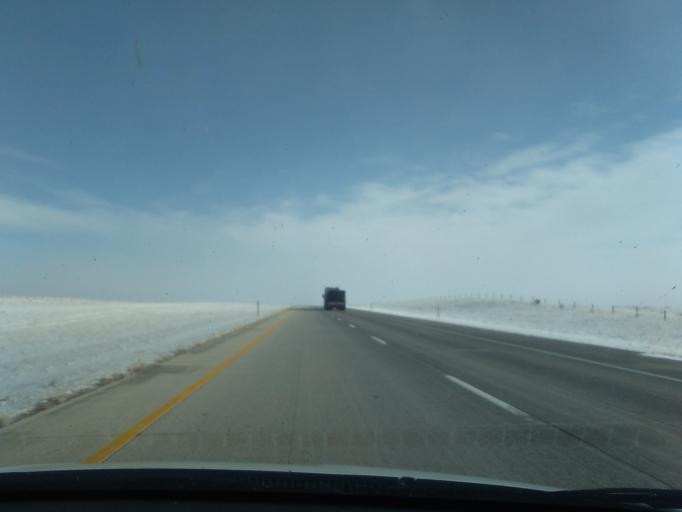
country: US
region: Wyoming
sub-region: Laramie County
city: Pine Bluffs
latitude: 41.1575
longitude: -104.3990
